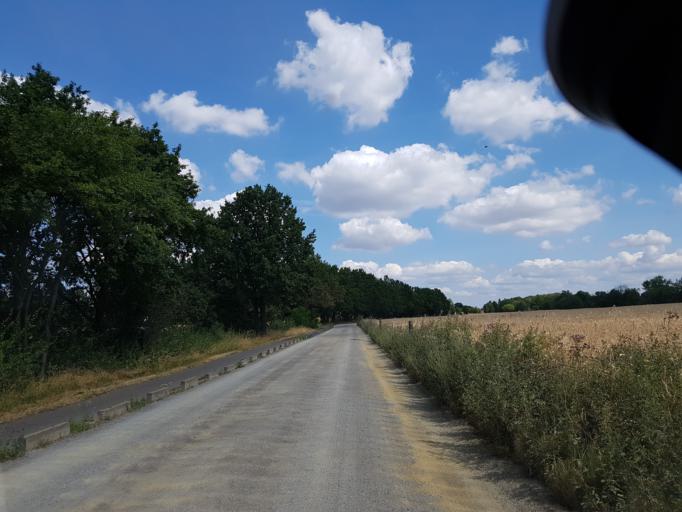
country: DE
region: Brandenburg
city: Cottbus
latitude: 51.7051
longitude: 14.3142
